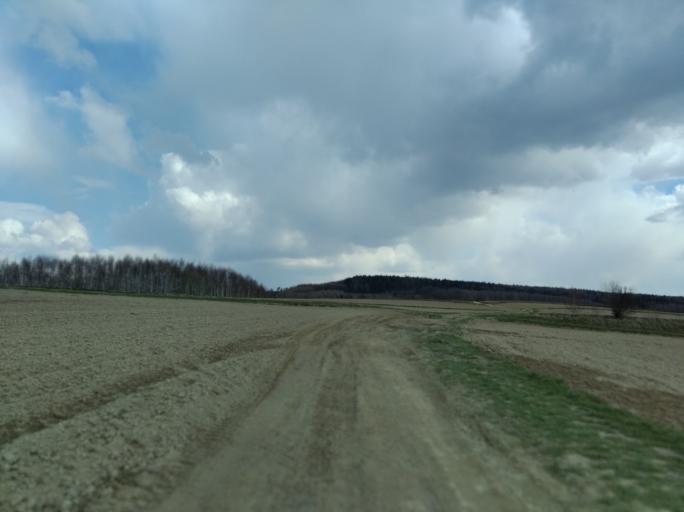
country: PL
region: Subcarpathian Voivodeship
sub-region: Powiat strzyzowski
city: Strzyzow
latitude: 49.9104
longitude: 21.7588
